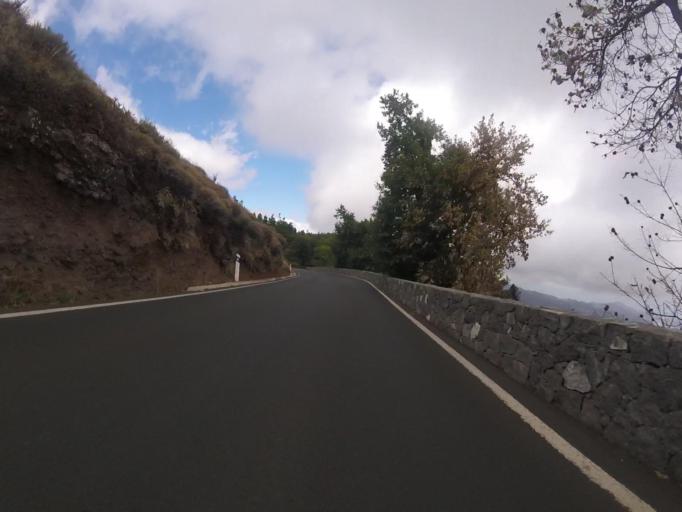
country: ES
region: Canary Islands
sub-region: Provincia de Las Palmas
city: San Bartolome
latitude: 27.9710
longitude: -15.5724
